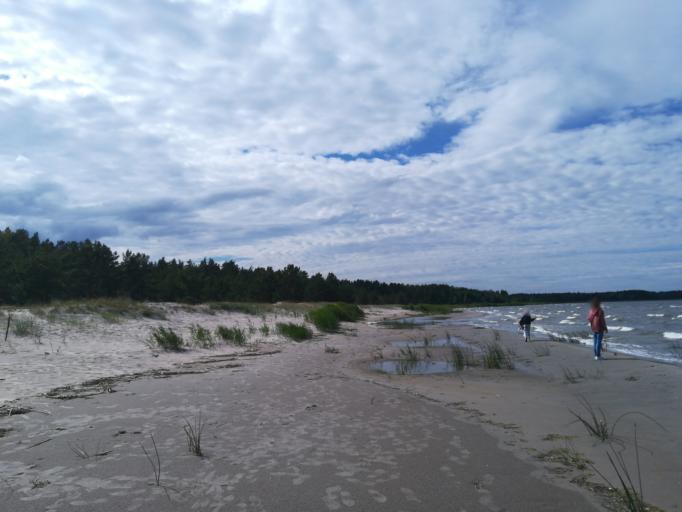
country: RU
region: Leningrad
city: Ust'-Luga
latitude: 59.6799
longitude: 28.2374
